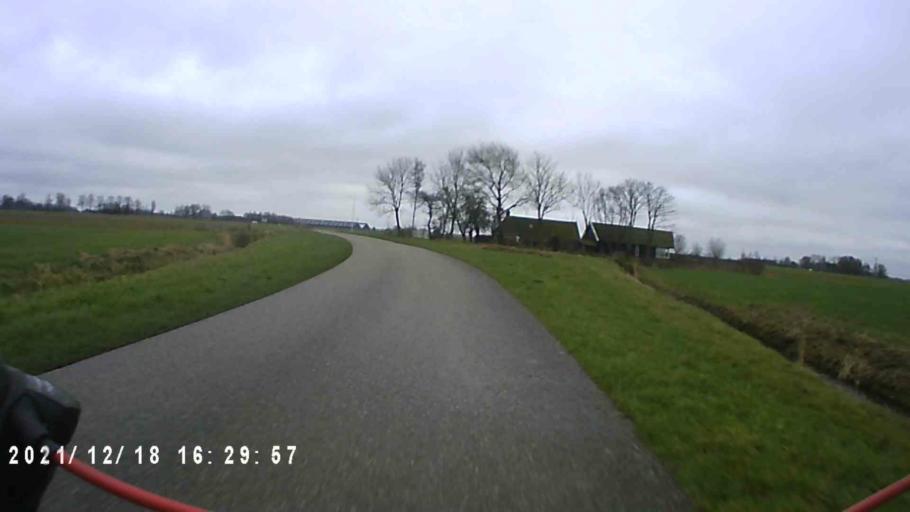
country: NL
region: Friesland
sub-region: Gemeente Dongeradeel
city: Dokkum
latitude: 53.3616
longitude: 6.0358
